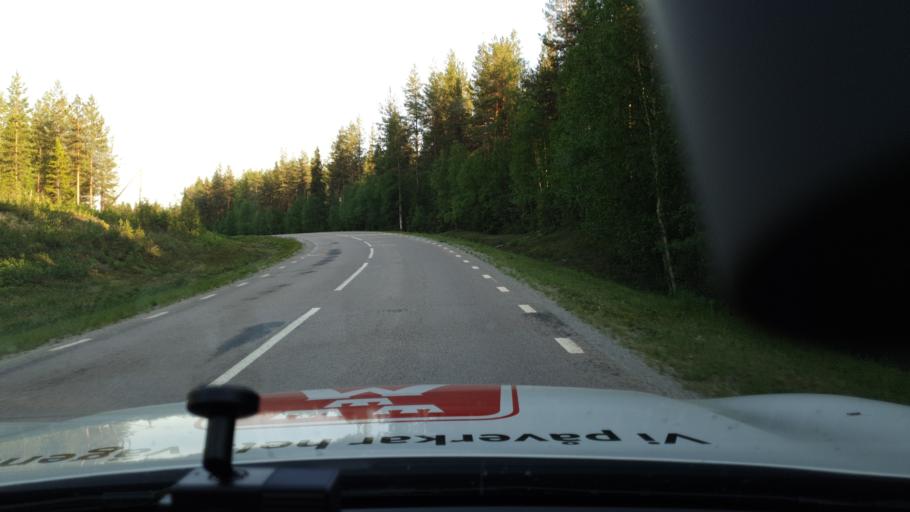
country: SE
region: Vaesterbotten
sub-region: Bjurholms Kommun
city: Bjurholm
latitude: 64.1820
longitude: 18.9003
